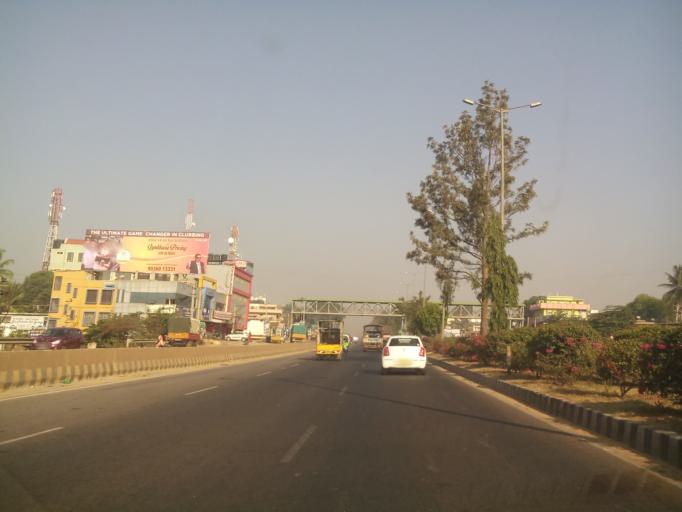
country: IN
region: Karnataka
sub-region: Bangalore Rural
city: Nelamangala
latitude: 13.0648
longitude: 77.4550
